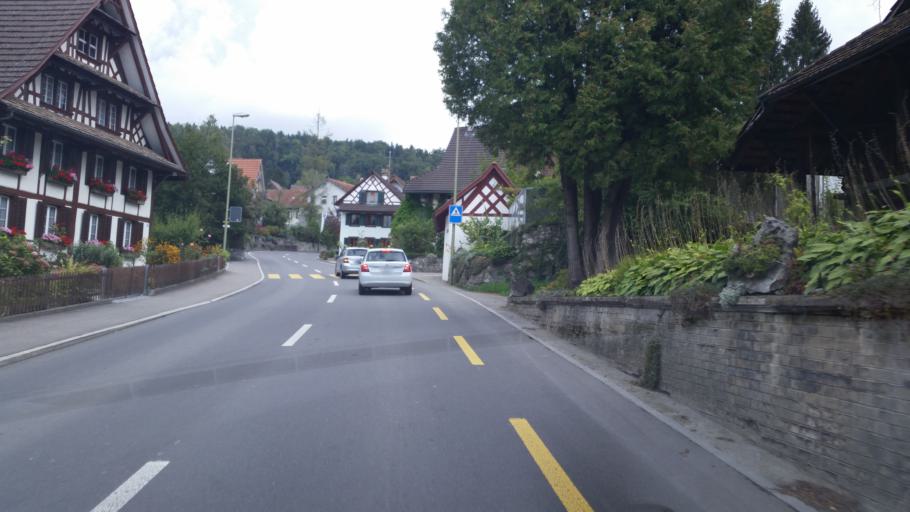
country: CH
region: Zurich
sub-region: Bezirk Affoltern
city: Mettmenstetten
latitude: 47.2456
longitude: 8.4671
